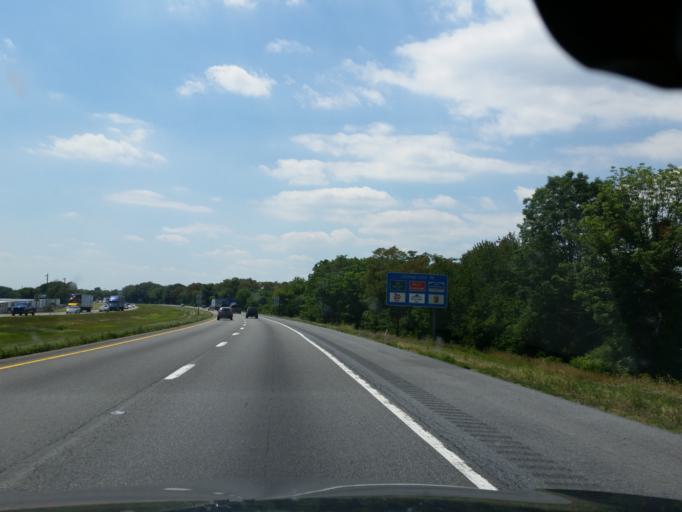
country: US
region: Pennsylvania
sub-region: Cumberland County
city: Schlusser
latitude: 40.2427
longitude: -77.1124
